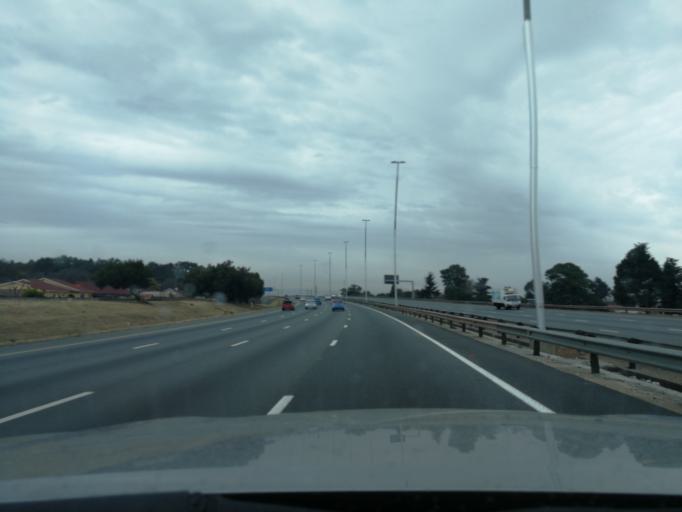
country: ZA
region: Gauteng
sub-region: Ekurhuleni Metropolitan Municipality
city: Germiston
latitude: -26.2767
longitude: 28.1492
